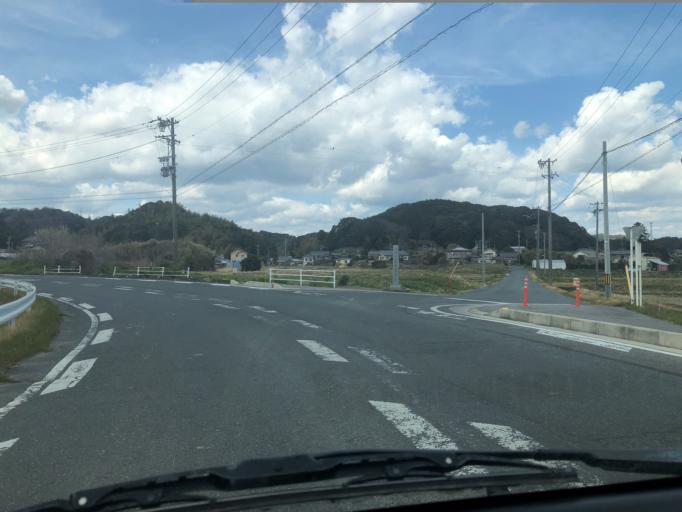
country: JP
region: Shizuoka
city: Mori
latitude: 34.8104
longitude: 137.9492
